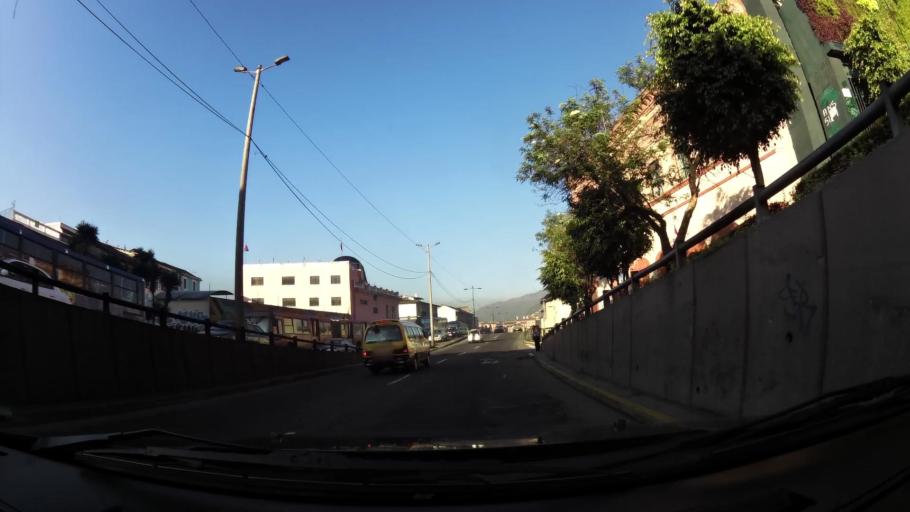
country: EC
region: Pichincha
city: Quito
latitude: -0.2183
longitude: -78.5061
